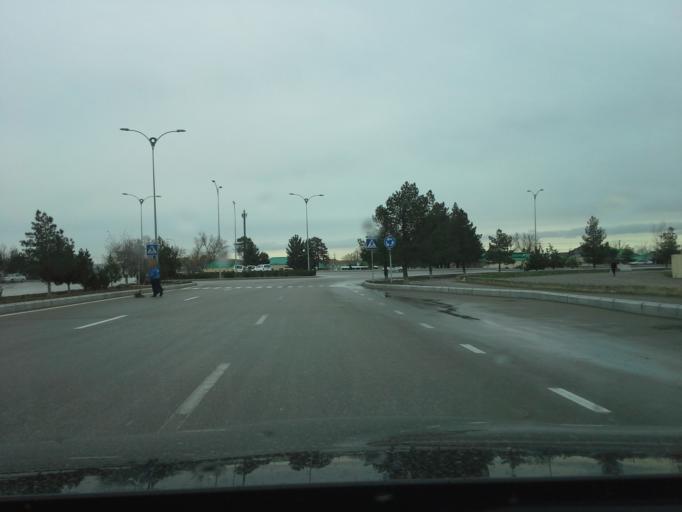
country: TM
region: Ahal
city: Abadan
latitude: 37.9634
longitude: 58.2221
